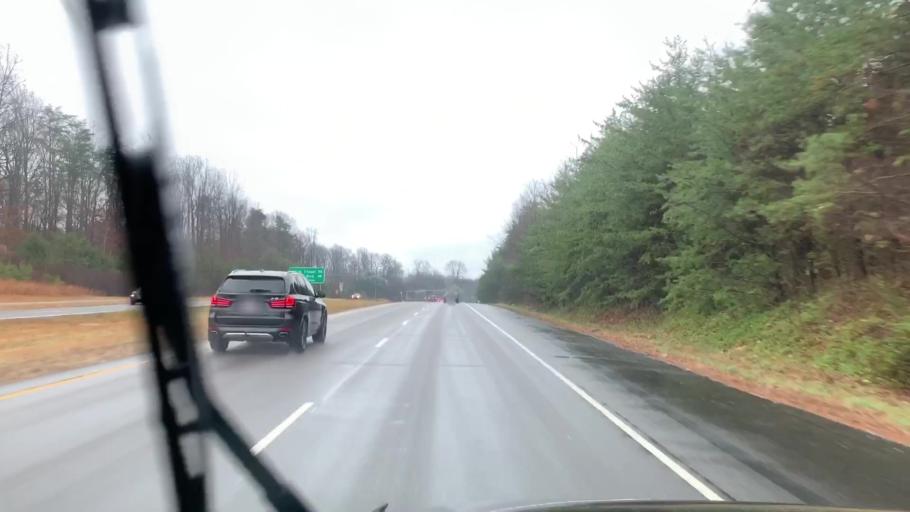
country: US
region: Virginia
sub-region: Fairfax County
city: Burke
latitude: 38.7451
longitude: -77.2903
